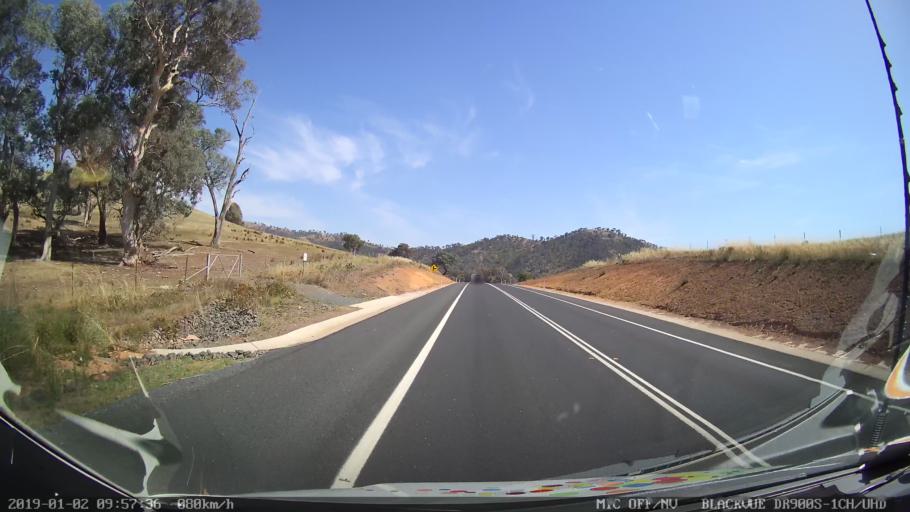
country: AU
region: New South Wales
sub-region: Tumut Shire
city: Tumut
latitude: -35.2035
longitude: 148.1654
